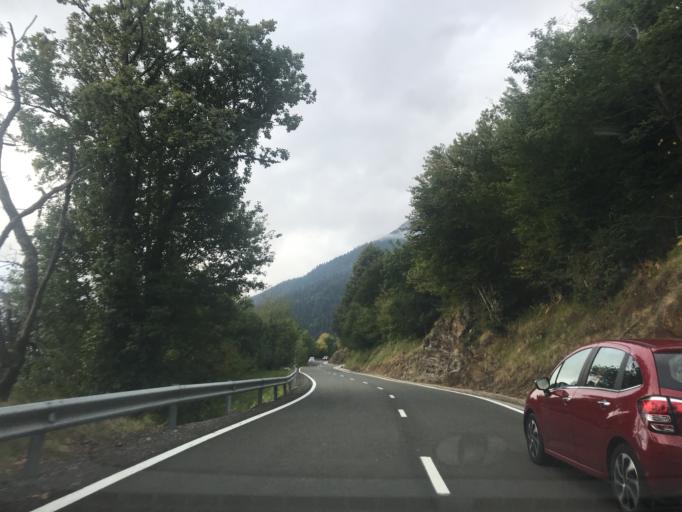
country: ES
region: Catalonia
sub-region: Provincia de Lleida
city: Les
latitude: 42.7745
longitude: 0.6776
